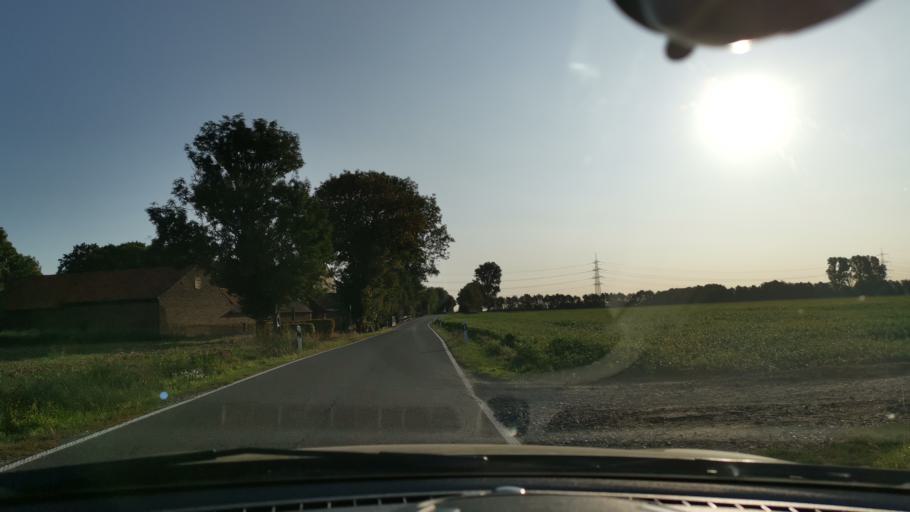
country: DE
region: North Rhine-Westphalia
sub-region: Regierungsbezirk Dusseldorf
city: Rommerskirchen
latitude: 51.0857
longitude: 6.6989
